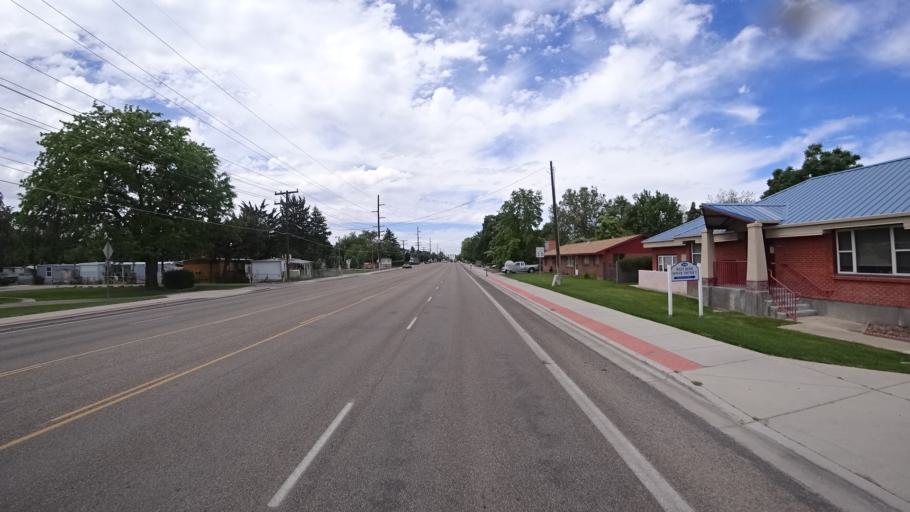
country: US
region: Idaho
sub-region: Ada County
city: Garden City
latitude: 43.6340
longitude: -116.2762
